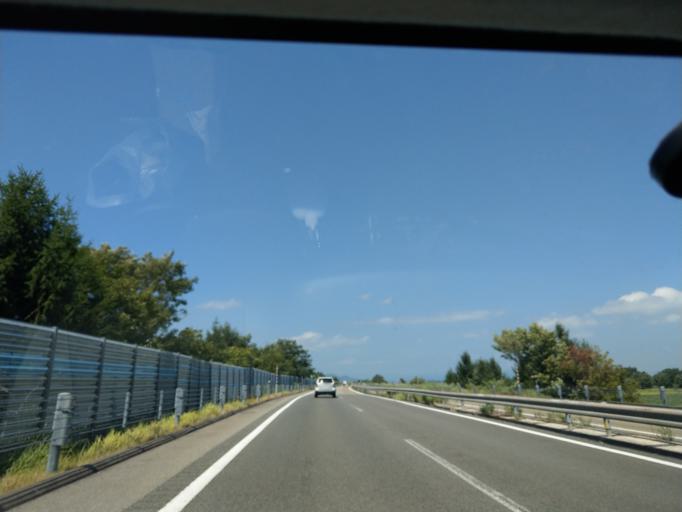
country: JP
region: Akita
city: Yokotemachi
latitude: 39.3616
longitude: 140.4887
